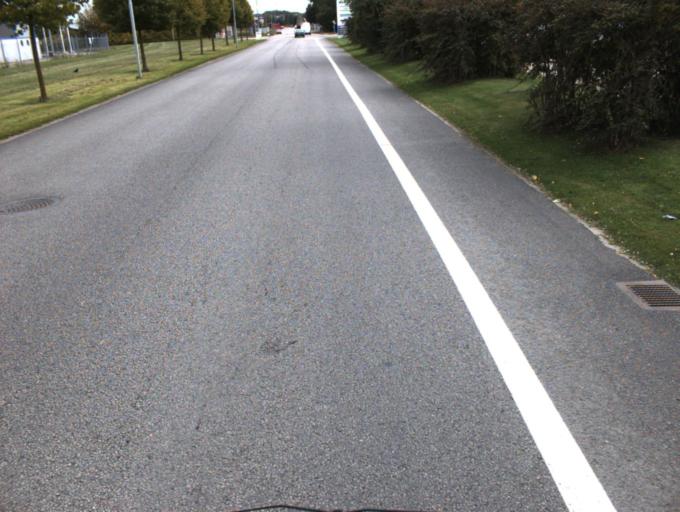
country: SE
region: Skane
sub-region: Helsingborg
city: Odakra
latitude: 56.0706
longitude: 12.7494
